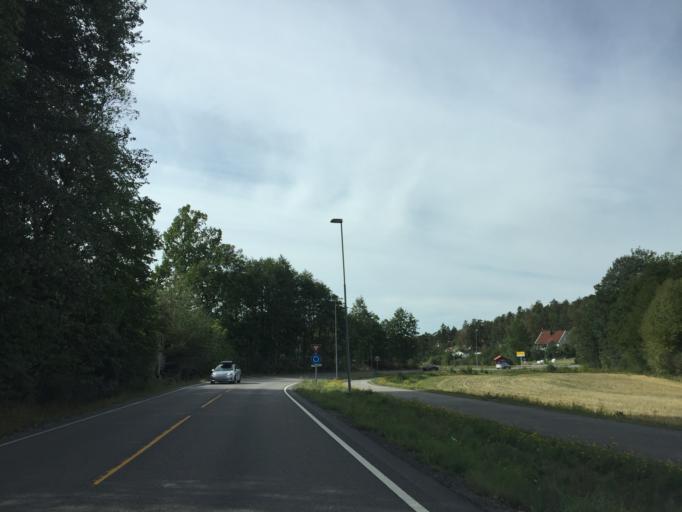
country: NO
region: Ostfold
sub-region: Moss
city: Moss
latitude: 59.5134
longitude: 10.6891
